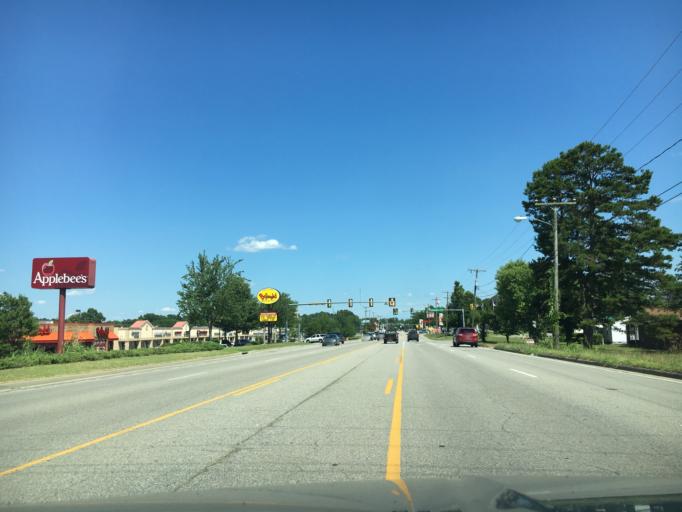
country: US
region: Virginia
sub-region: Halifax County
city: Halifax
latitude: 36.7348
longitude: -78.9151
